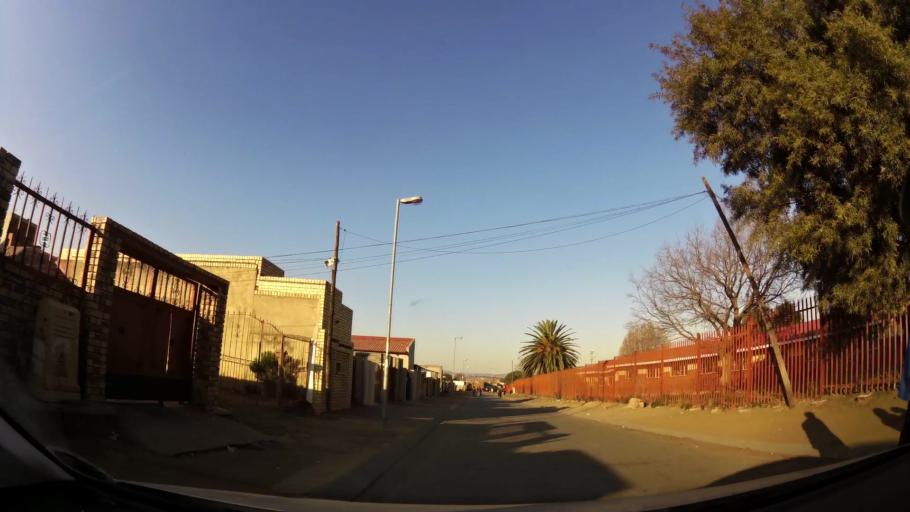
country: ZA
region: Gauteng
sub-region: City of Johannesburg Metropolitan Municipality
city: Soweto
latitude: -26.2510
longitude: 27.8792
